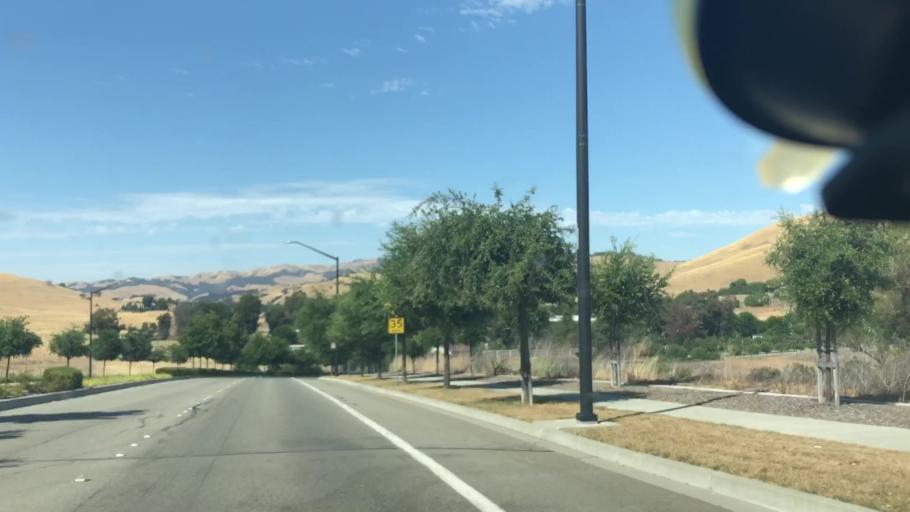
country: US
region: California
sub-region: Alameda County
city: Dublin
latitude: 37.7481
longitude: -121.8768
